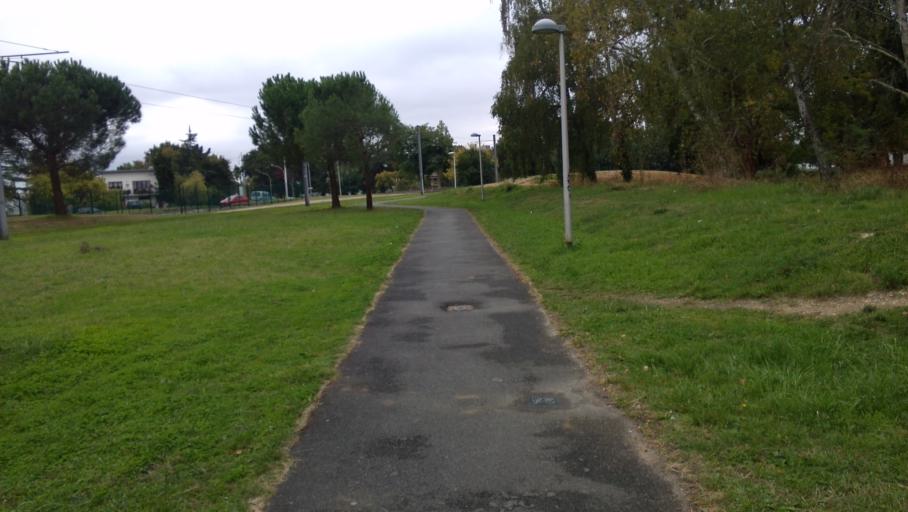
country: FR
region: Aquitaine
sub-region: Departement de la Gironde
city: Talence
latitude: 44.7984
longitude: -0.6126
